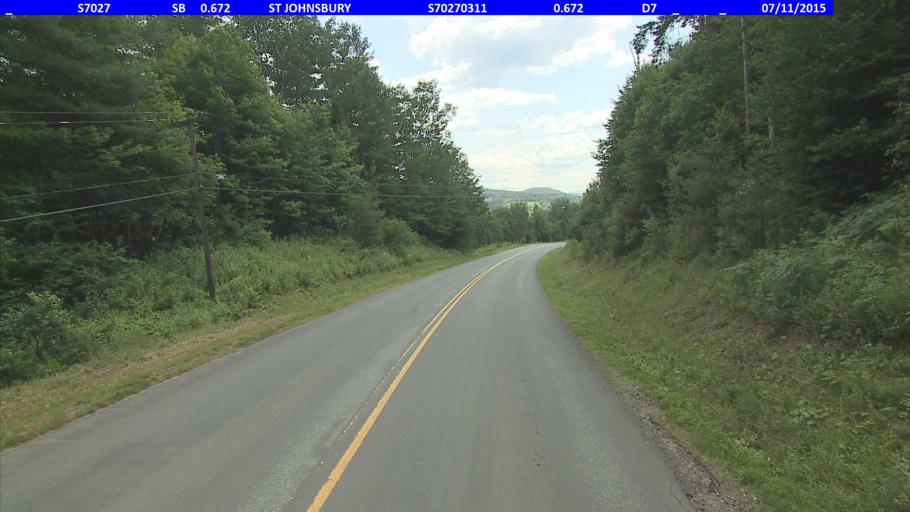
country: US
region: Vermont
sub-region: Caledonia County
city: St Johnsbury
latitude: 44.4573
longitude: -71.9457
